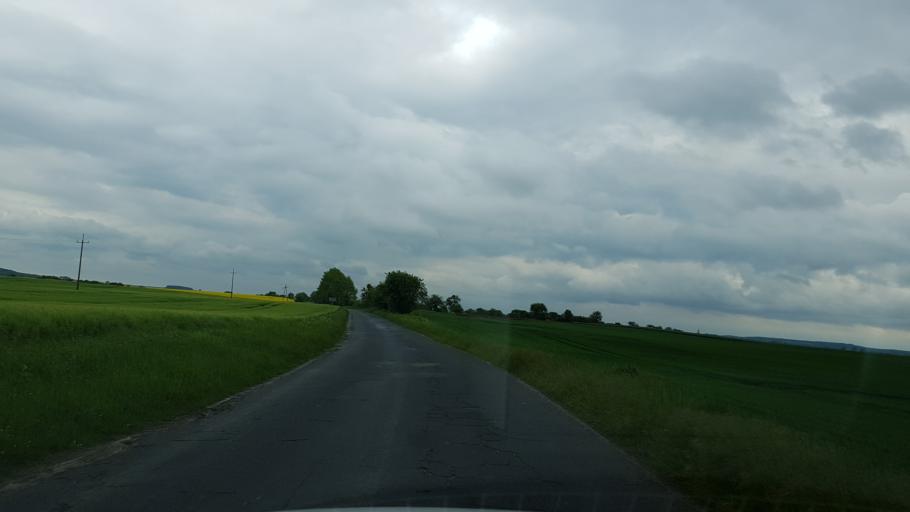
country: PL
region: West Pomeranian Voivodeship
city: Trzcinsko Zdroj
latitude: 52.9951
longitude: 14.5785
